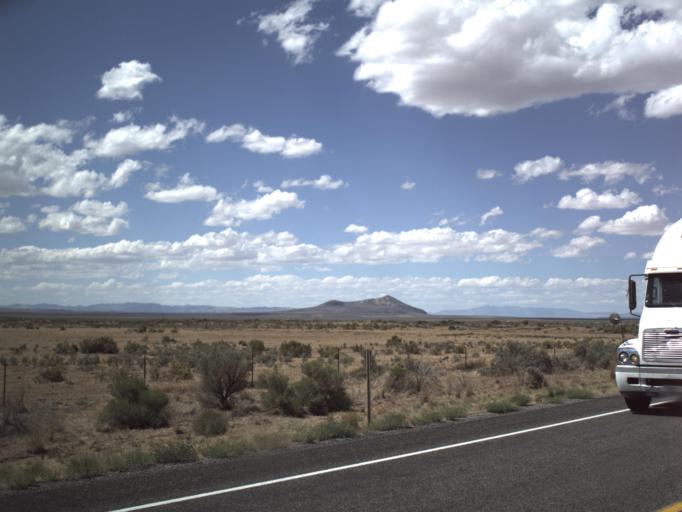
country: US
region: Utah
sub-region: Millard County
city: Fillmore
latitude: 39.1445
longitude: -112.3841
